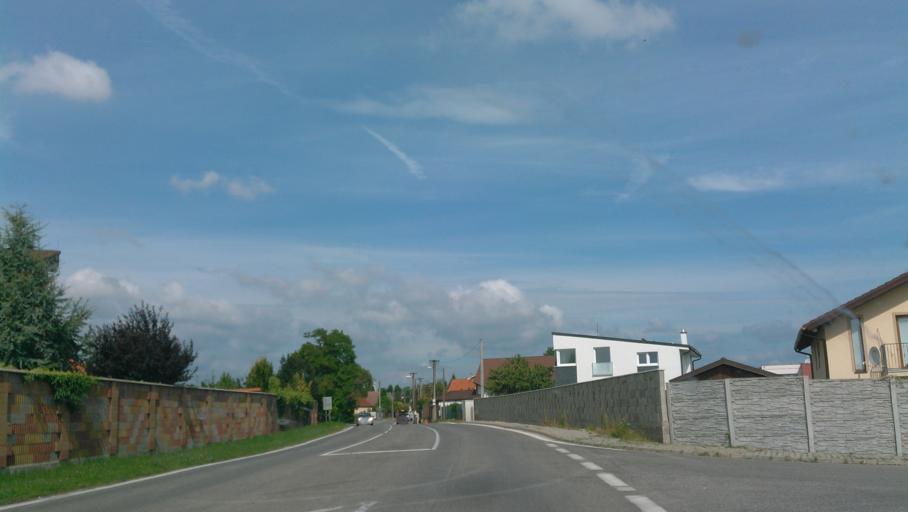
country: SK
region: Bratislavsky
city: Dunajska Luzna
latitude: 48.1483
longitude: 17.2207
